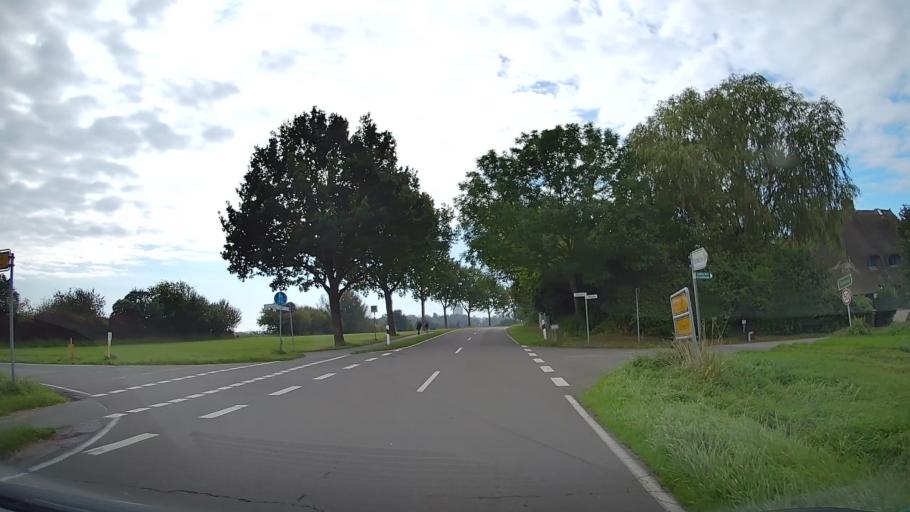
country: DE
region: Schleswig-Holstein
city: Panker
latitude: 54.3427
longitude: 10.6042
